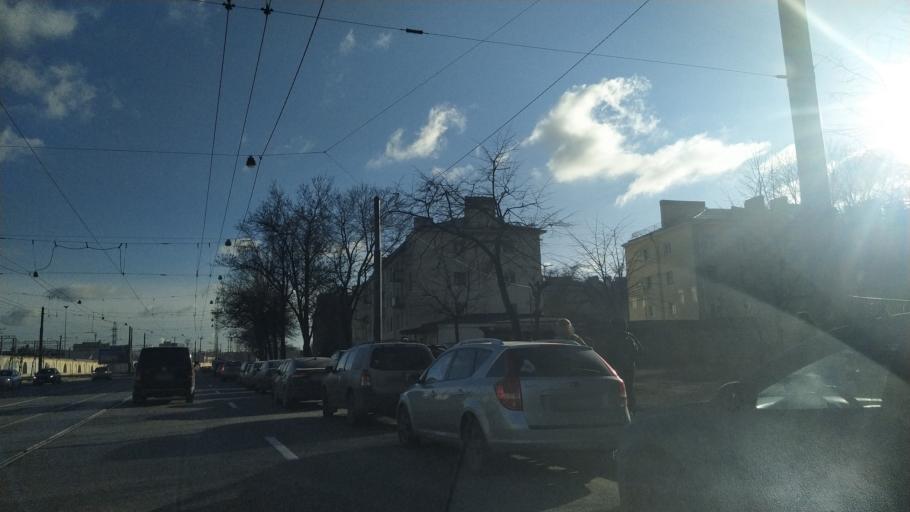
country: RU
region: Leningrad
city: Sampsonievskiy
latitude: 59.9744
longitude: 30.3464
